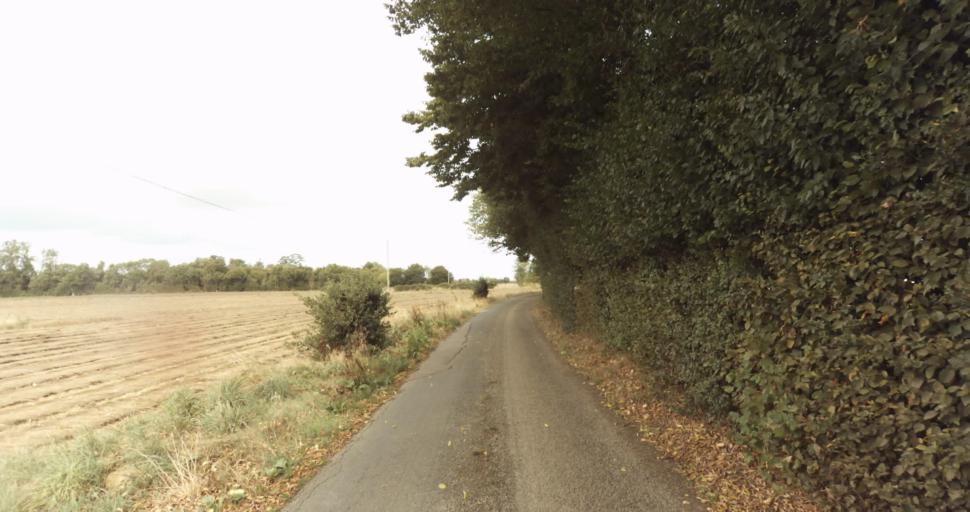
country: FR
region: Lower Normandy
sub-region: Departement de l'Orne
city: Gace
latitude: 48.8847
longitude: 0.3616
